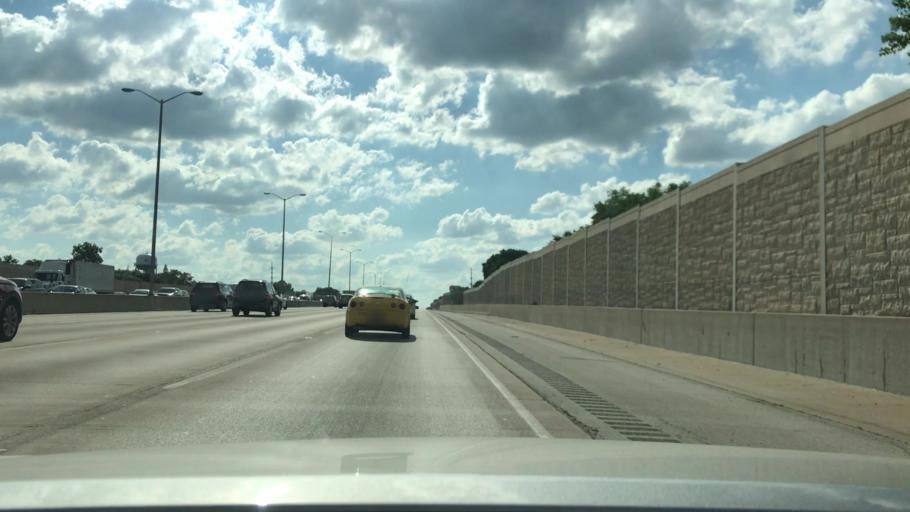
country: US
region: Illinois
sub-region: DuPage County
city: Lisle
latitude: 41.8060
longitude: -88.0896
